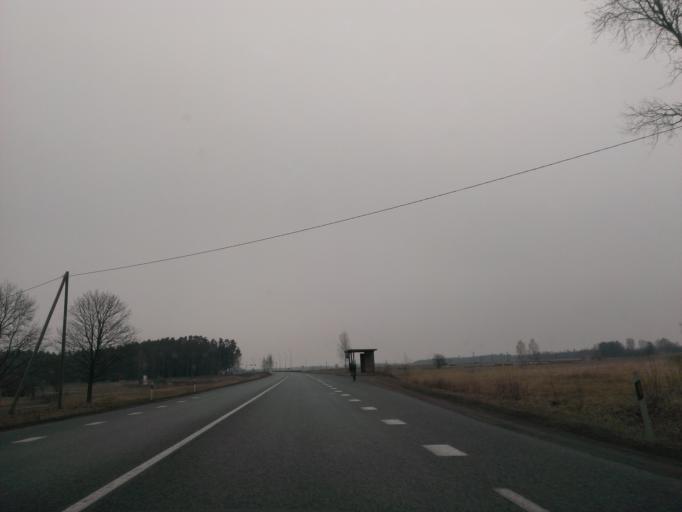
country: LV
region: Saulkrastu
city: Saulkrasti
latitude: 57.4040
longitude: 24.4303
